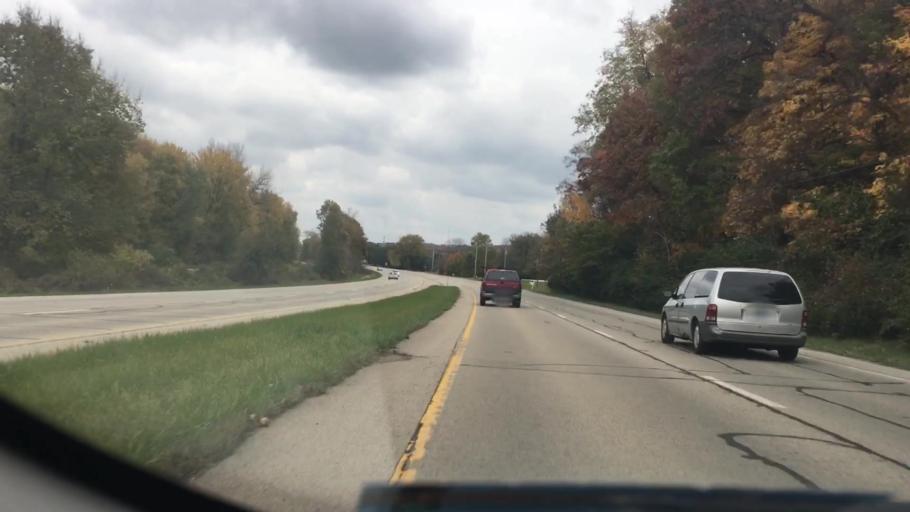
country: US
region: Illinois
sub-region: Peoria County
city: Peoria Heights
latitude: 40.7785
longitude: -89.5769
